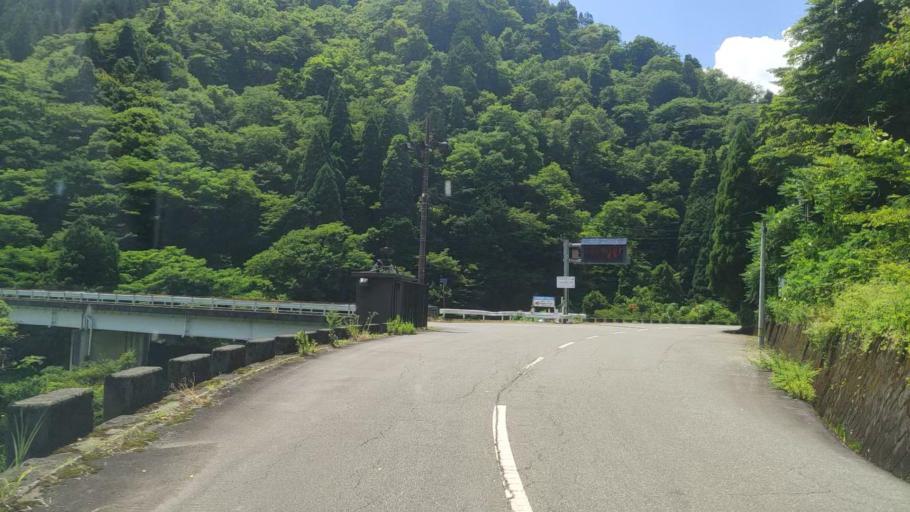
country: JP
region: Fukui
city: Ono
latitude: 35.8743
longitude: 136.5028
